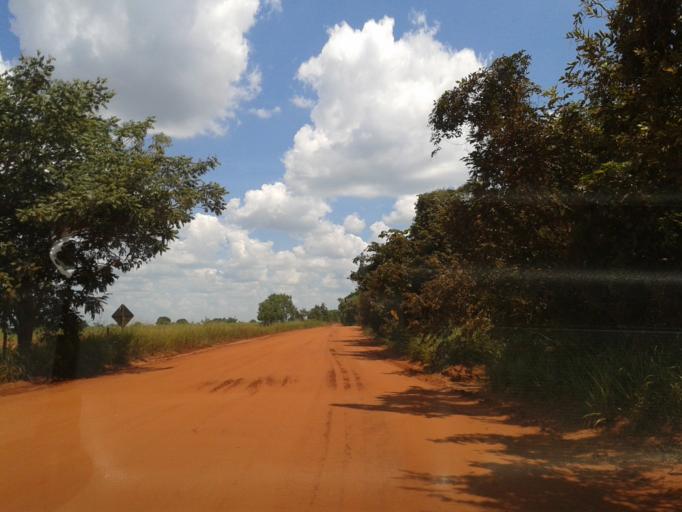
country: BR
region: Minas Gerais
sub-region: Ituiutaba
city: Ituiutaba
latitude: -19.0829
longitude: -49.7314
